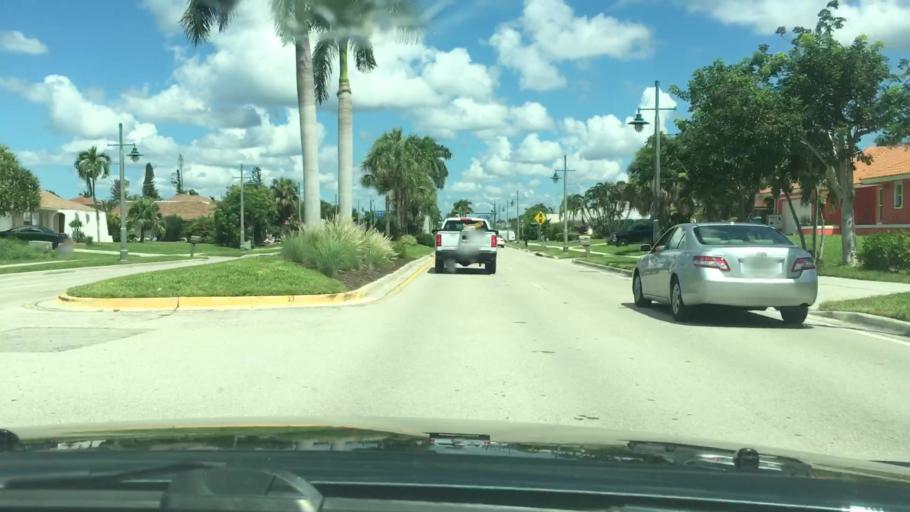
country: US
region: Florida
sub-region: Collier County
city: Marco
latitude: 25.9461
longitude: -81.7327
